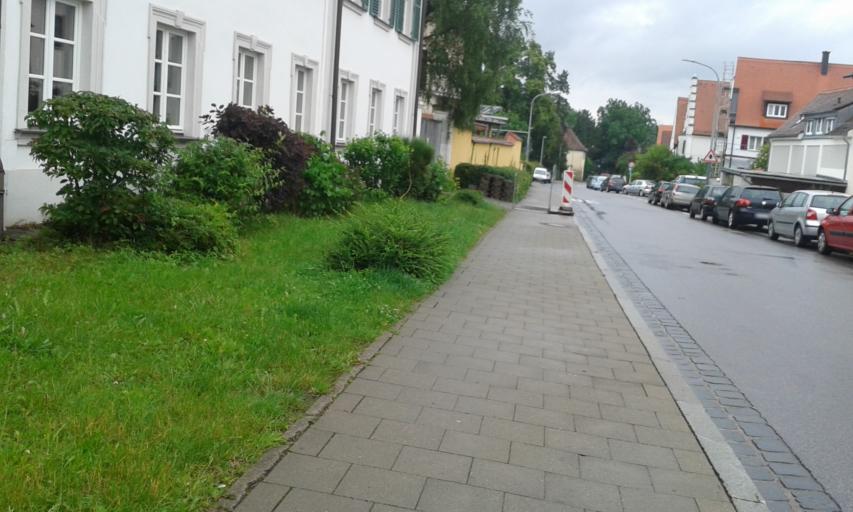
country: DE
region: Bavaria
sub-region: Upper Franconia
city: Bamberg
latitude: 49.8820
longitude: 10.8861
